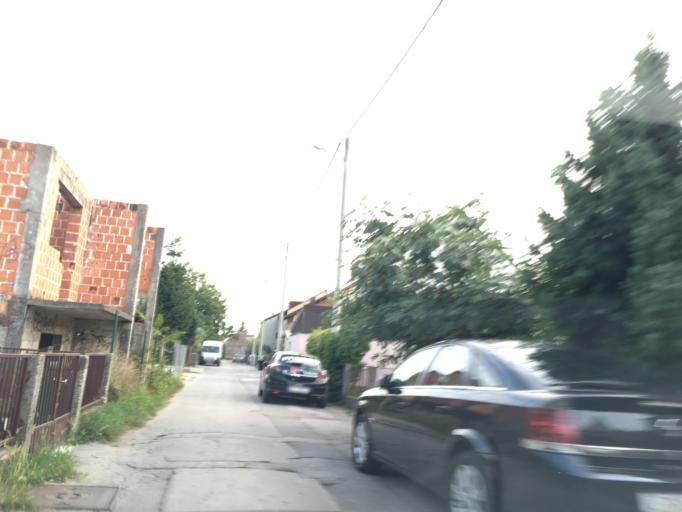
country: HR
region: Grad Zagreb
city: Jankomir
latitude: 45.8007
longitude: 15.9243
